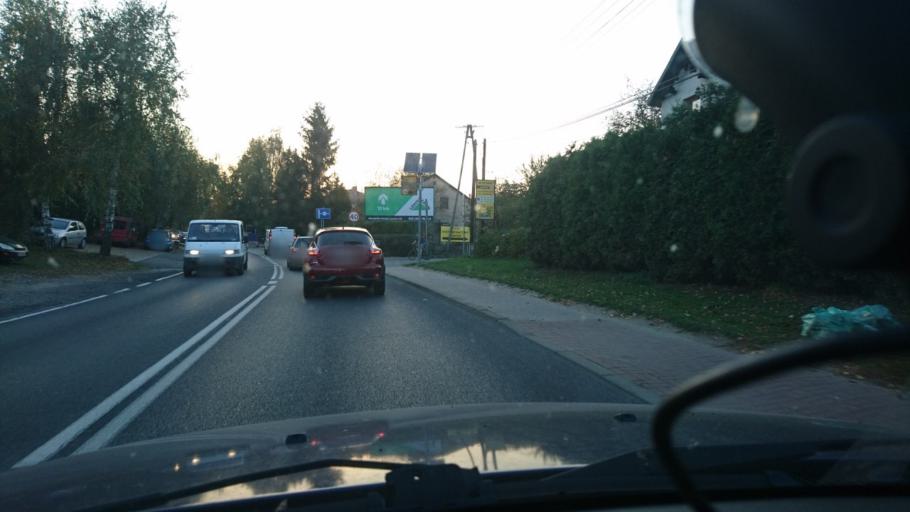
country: PL
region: Silesian Voivodeship
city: Janowice
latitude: 49.8509
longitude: 19.0952
